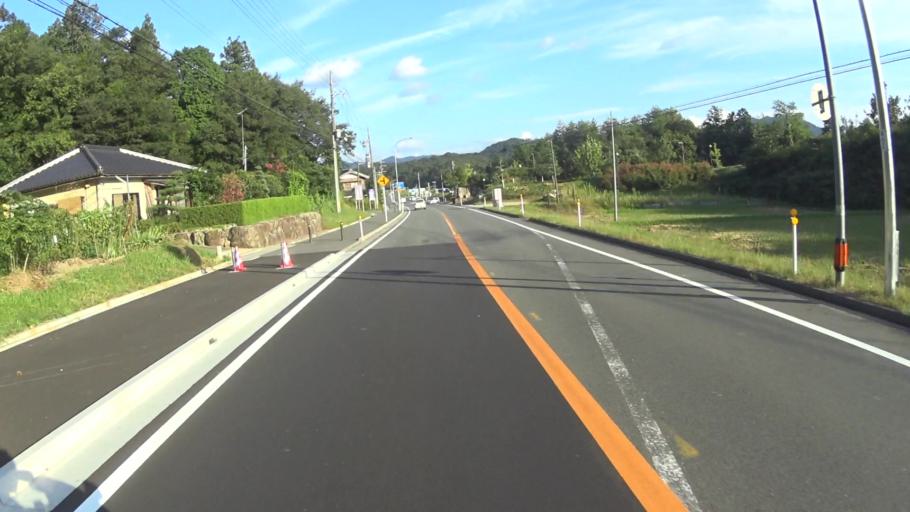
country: JP
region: Hyogo
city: Toyooka
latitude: 35.5908
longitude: 134.9399
